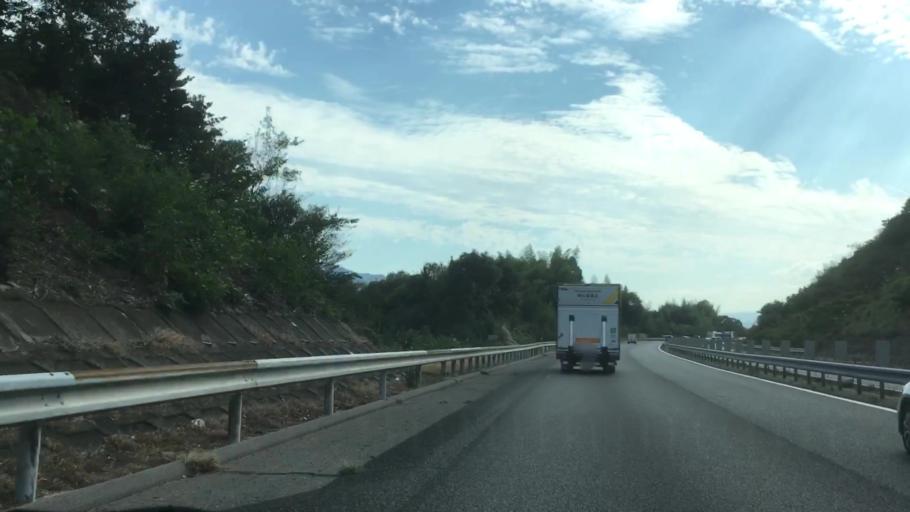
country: JP
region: Hiroshima
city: Ono-hara
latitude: 34.3086
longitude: 132.2800
